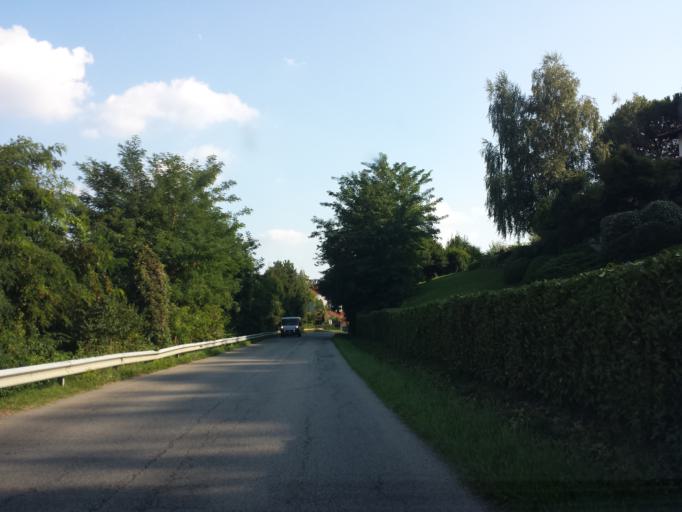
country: IT
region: Lombardy
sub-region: Provincia di Varese
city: Leggiuno
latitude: 45.8718
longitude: 8.6098
